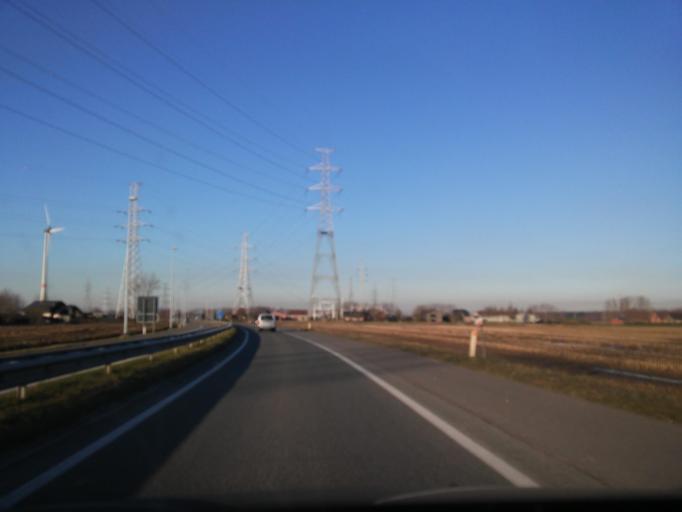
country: BE
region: Flanders
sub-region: Provincie Oost-Vlaanderen
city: Eeklo
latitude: 51.2004
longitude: 3.5349
